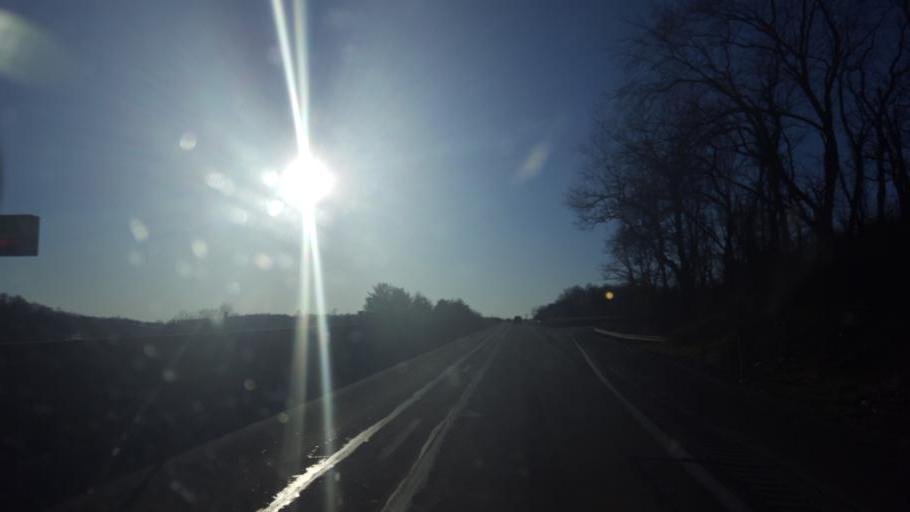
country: US
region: Pennsylvania
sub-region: Westmoreland County
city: New Stanton
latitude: 40.2114
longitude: -79.6625
